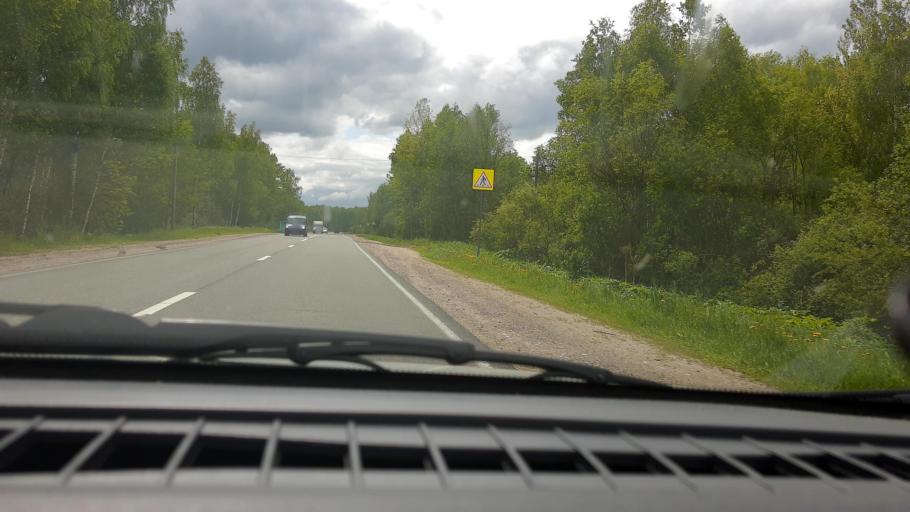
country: RU
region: Nizjnij Novgorod
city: Sukhobezvodnoye
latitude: 56.8461
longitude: 44.7480
